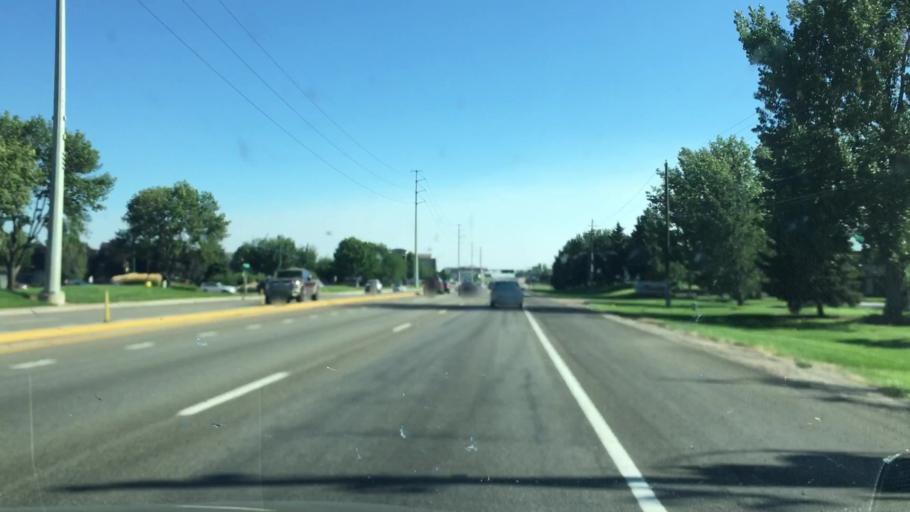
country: US
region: Idaho
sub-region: Ada County
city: Meridian
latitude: 43.6156
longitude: -116.3547
